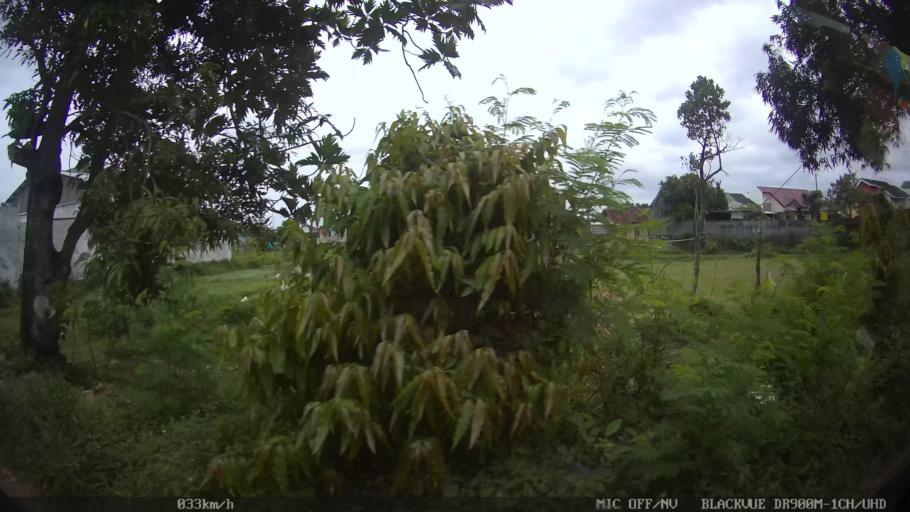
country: ID
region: Daerah Istimewa Yogyakarta
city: Depok
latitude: -7.8128
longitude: 110.4176
